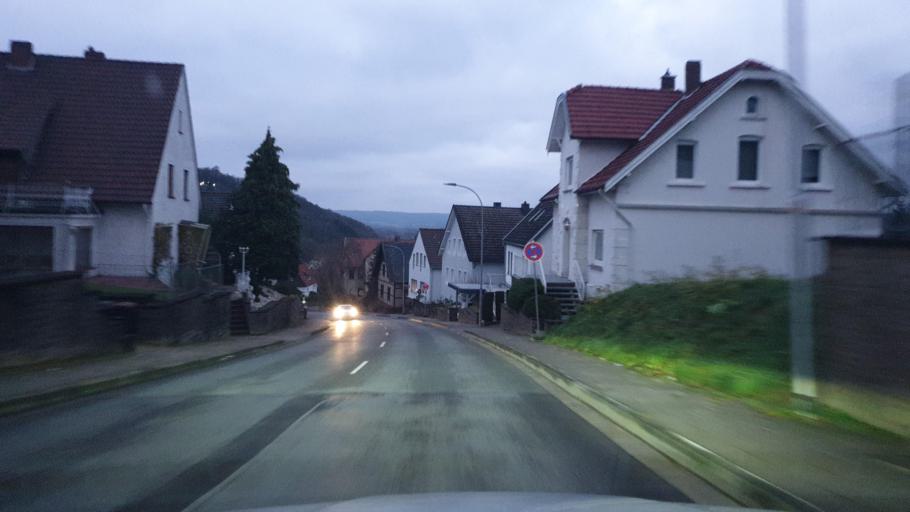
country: DE
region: North Rhine-Westphalia
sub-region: Regierungsbezirk Detmold
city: Vlotho
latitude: 52.1641
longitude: 8.8666
